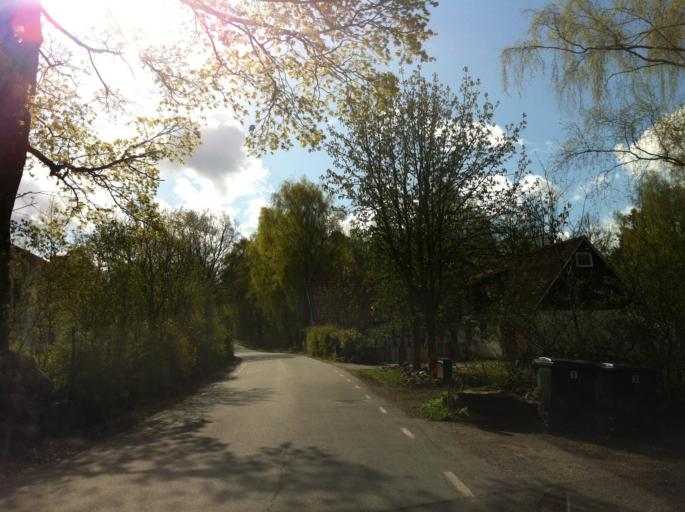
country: SE
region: Skane
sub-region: Hoors Kommun
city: Hoeoer
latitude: 55.9134
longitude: 13.4832
